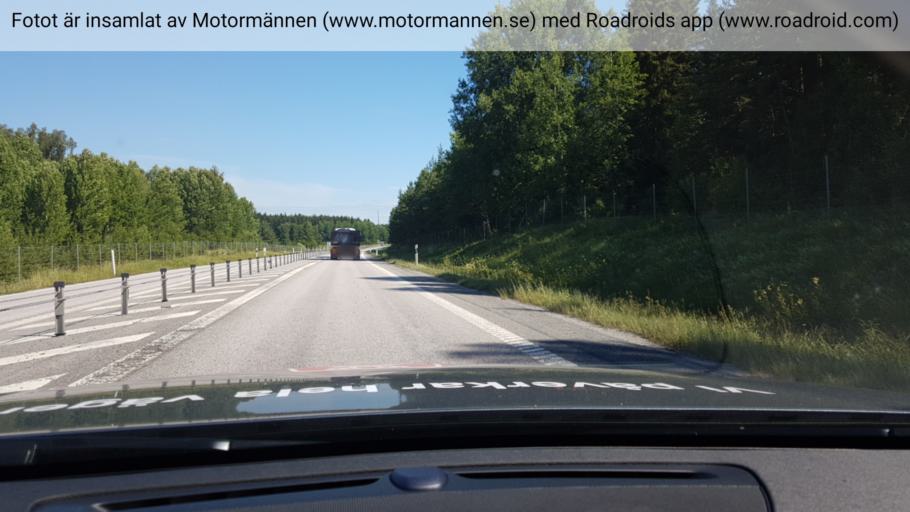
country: SE
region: Stockholm
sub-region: Vallentuna Kommun
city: Vallentuna
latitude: 59.5138
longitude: 18.1771
